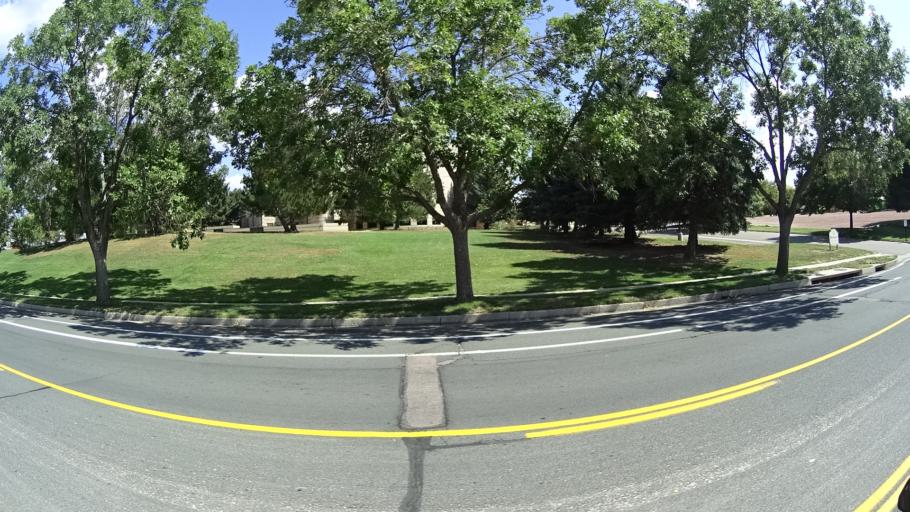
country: US
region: Colorado
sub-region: El Paso County
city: Cimarron Hills
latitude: 38.8848
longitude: -104.7386
